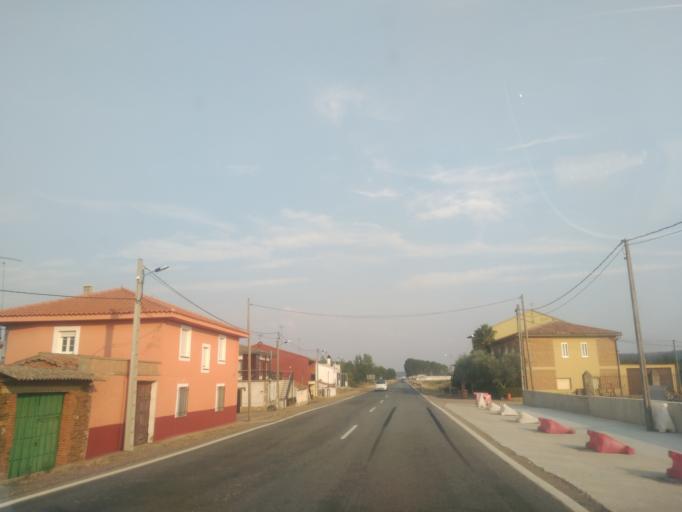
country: ES
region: Castille and Leon
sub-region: Provincia de Zamora
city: Pozuelo de Tabara
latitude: 41.7839
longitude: -5.8938
